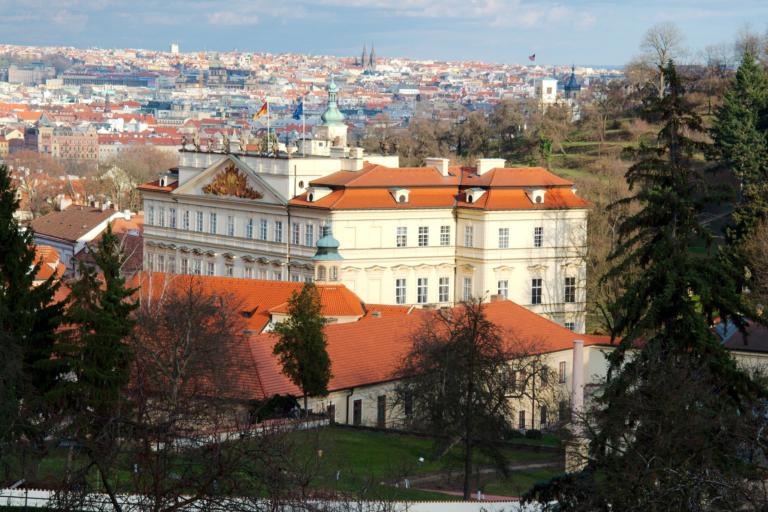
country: CZ
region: Praha
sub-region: Praha 1
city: Mala Strana
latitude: 50.0882
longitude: 14.3946
